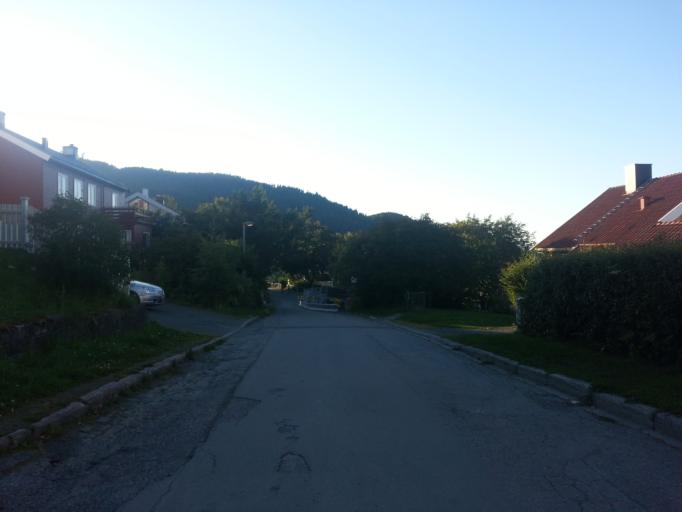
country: NO
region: Sor-Trondelag
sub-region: Trondheim
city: Trondheim
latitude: 63.4270
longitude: 10.3625
